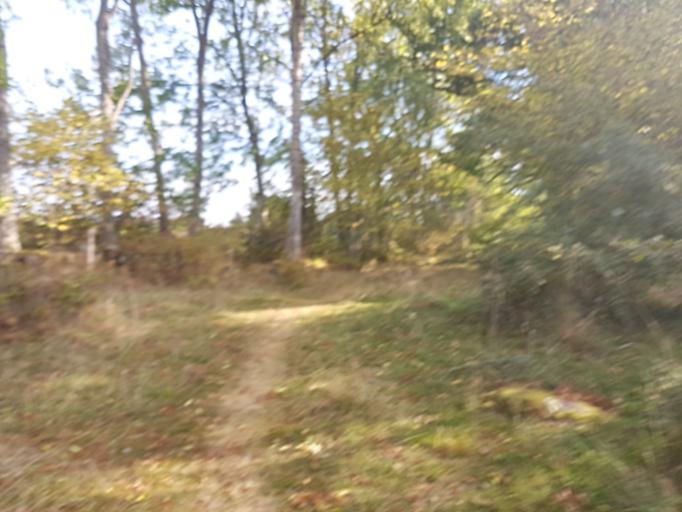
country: SE
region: Kronoberg
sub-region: Vaxjo Kommun
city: Vaexjoe
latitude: 56.8479
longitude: 14.8338
